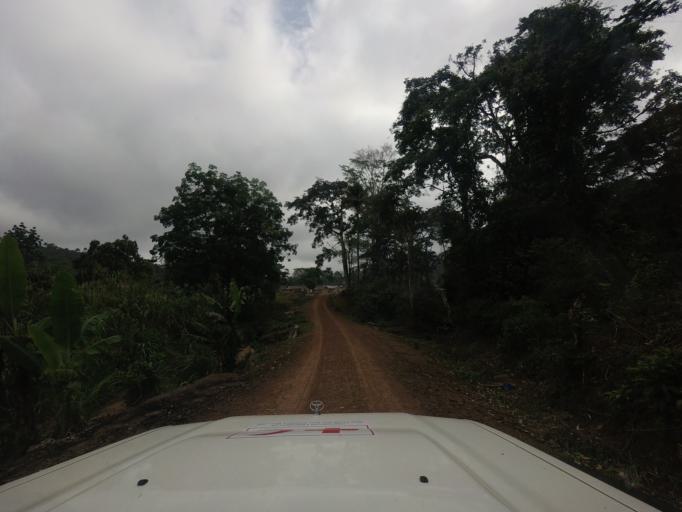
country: LR
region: Lofa
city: Voinjama
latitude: 8.4615
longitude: -9.7908
